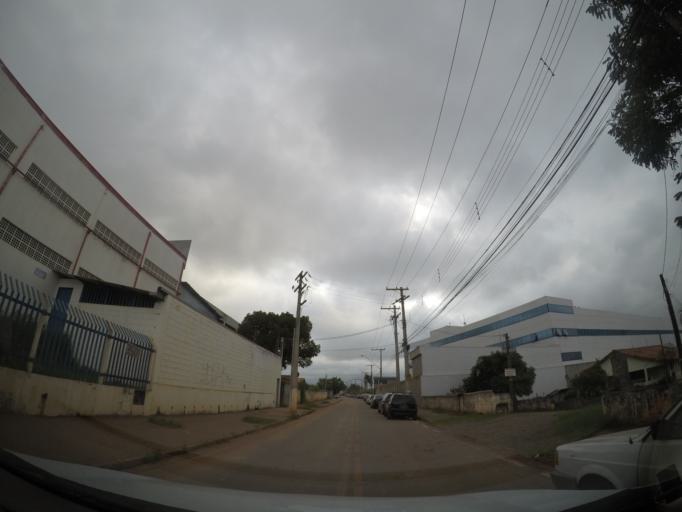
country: BR
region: Sao Paulo
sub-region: Aruja
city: Aruja
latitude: -23.4081
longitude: -46.3617
